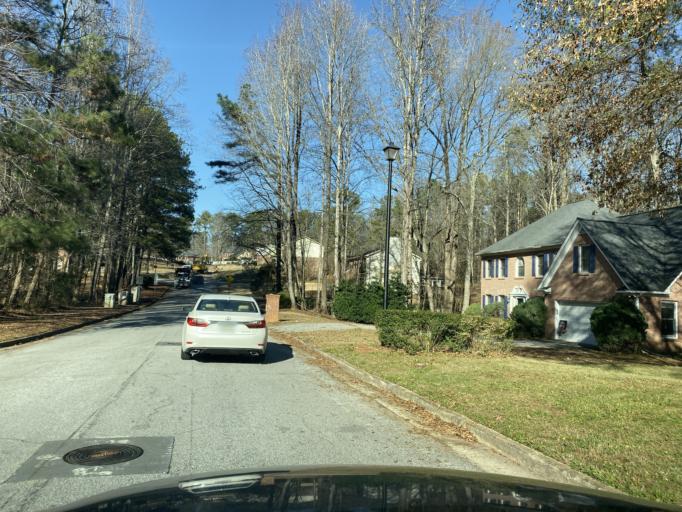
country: US
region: Georgia
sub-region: DeKalb County
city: Pine Mountain
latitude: 33.6776
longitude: -84.1571
